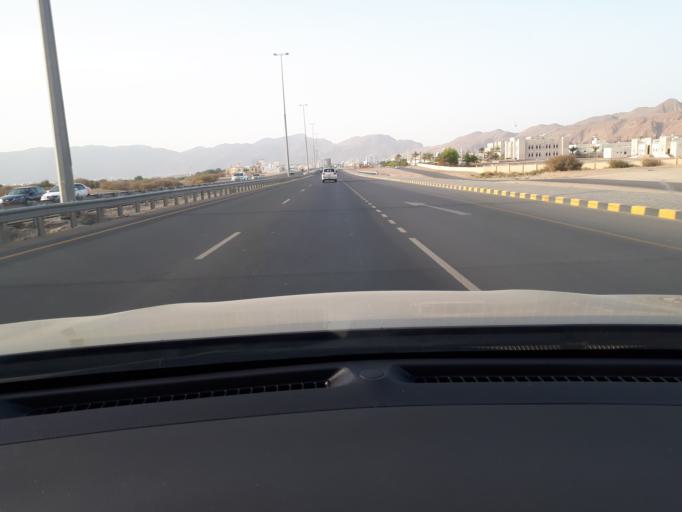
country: OM
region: Muhafazat Masqat
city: Bawshar
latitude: 23.4865
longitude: 58.4995
